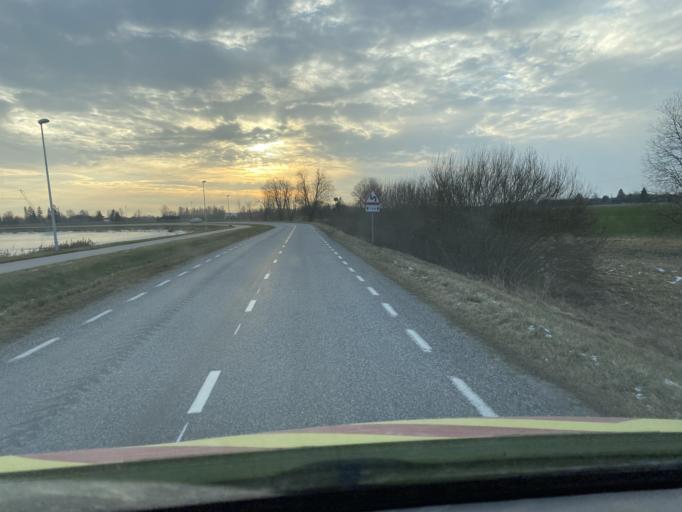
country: EE
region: Jogevamaa
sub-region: Poltsamaa linn
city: Poltsamaa
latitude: 58.6194
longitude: 25.9819
